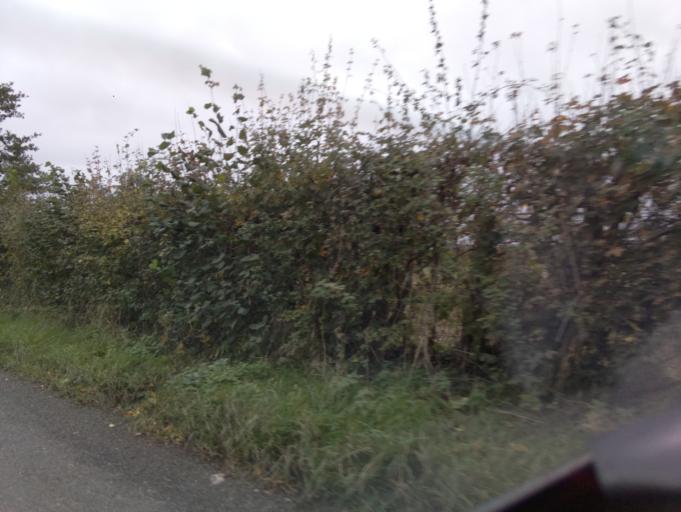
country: GB
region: England
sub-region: Somerset
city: Ilminster
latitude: 50.9424
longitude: -2.9490
